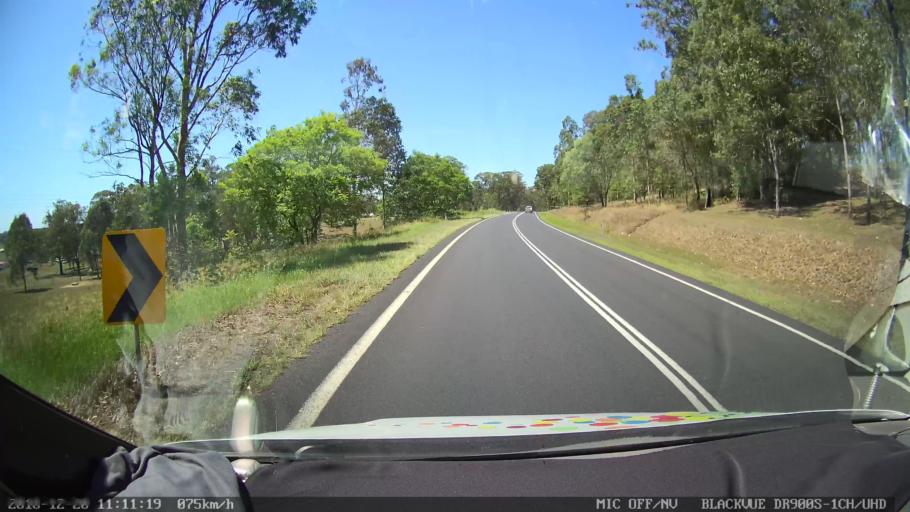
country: AU
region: New South Wales
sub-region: Richmond Valley
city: Casino
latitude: -28.9595
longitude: 153.0136
